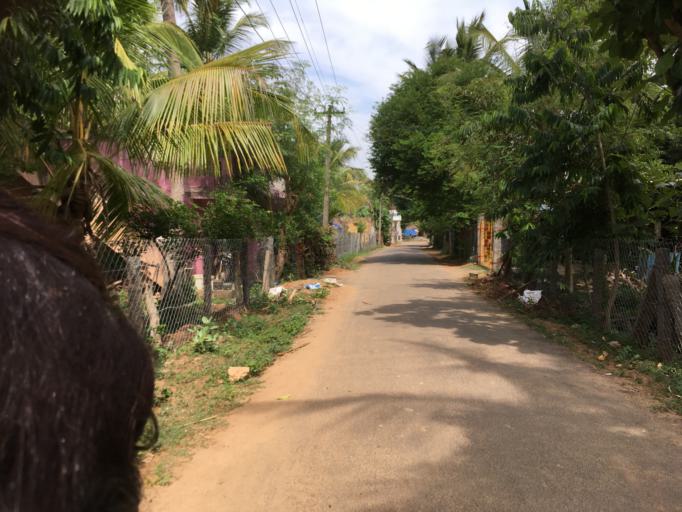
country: IN
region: Tamil Nadu
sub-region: Villupuram
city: Auroville
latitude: 12.0117
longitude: 79.7975
